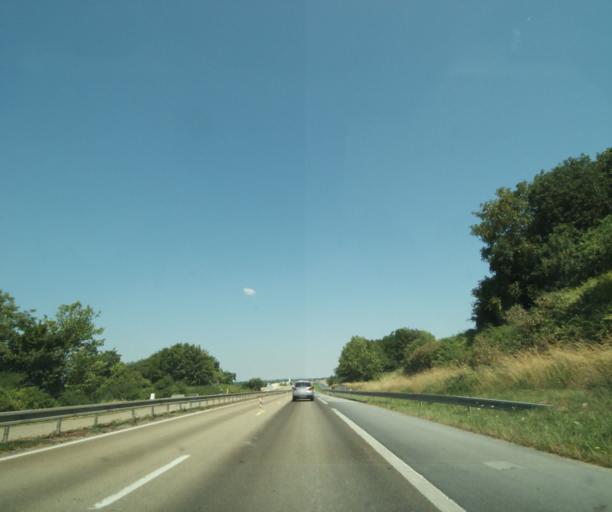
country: FR
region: Champagne-Ardenne
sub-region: Departement de la Marne
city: Sarry
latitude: 48.8754
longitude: 4.4693
